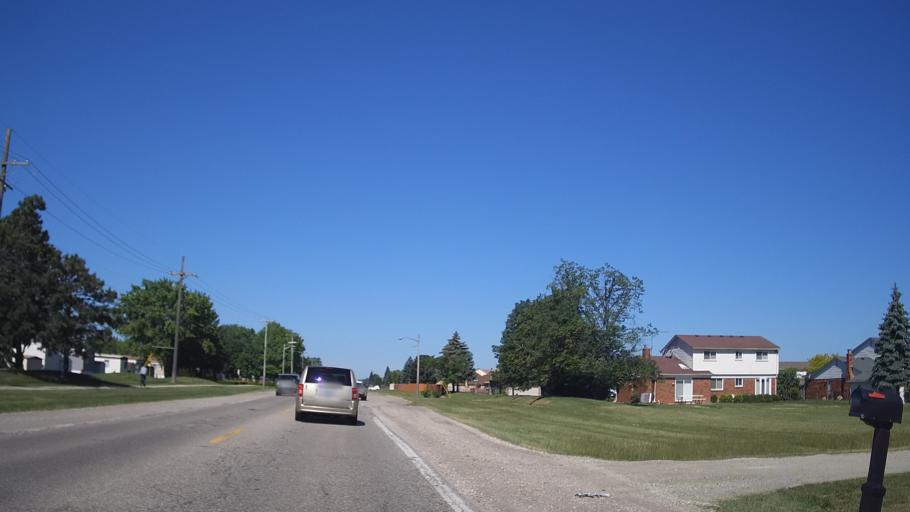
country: US
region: Michigan
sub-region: Macomb County
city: Sterling Heights
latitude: 42.5941
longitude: -83.0560
